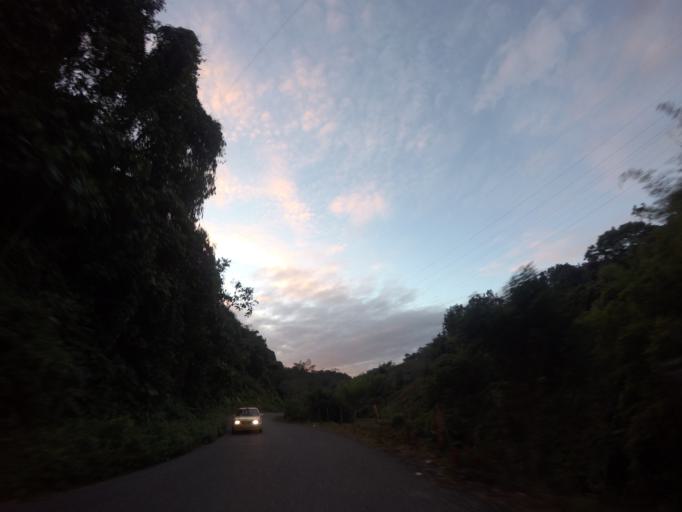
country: CO
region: Caldas
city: Manzanares
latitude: 5.2712
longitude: -75.1267
